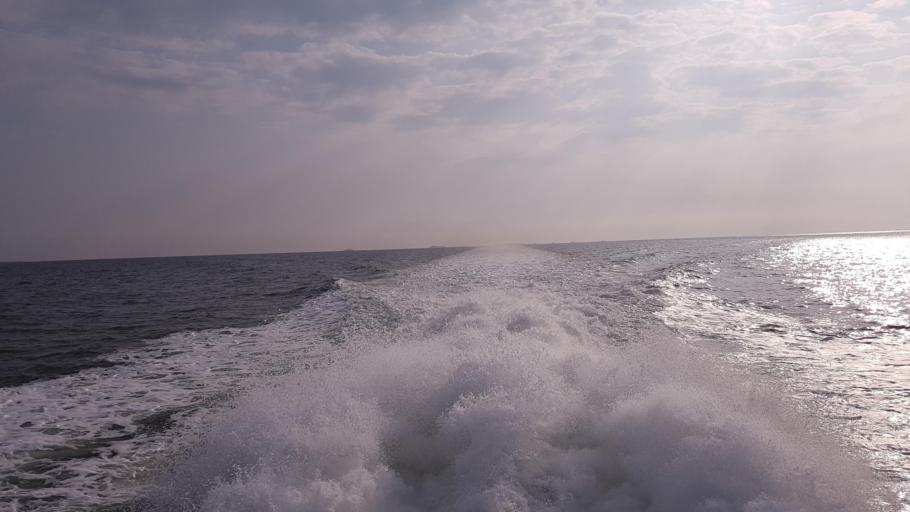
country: DE
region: Schleswig-Holstein
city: Grode
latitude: 54.6043
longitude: 8.6635
